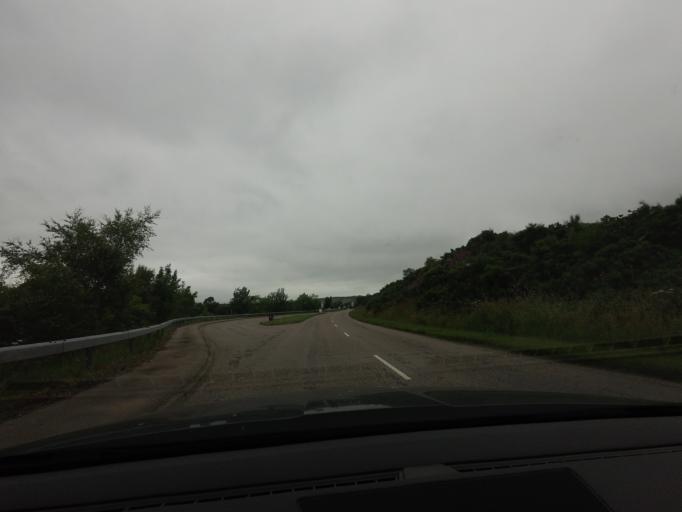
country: GB
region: Scotland
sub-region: Highland
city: Alness
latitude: 58.0175
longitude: -4.4028
